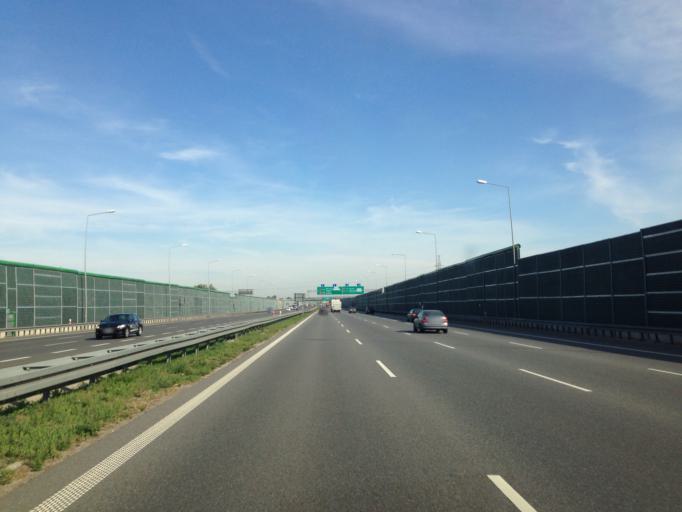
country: PL
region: Masovian Voivodeship
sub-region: Powiat pruszkowski
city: Piastow
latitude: 52.1950
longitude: 20.8230
